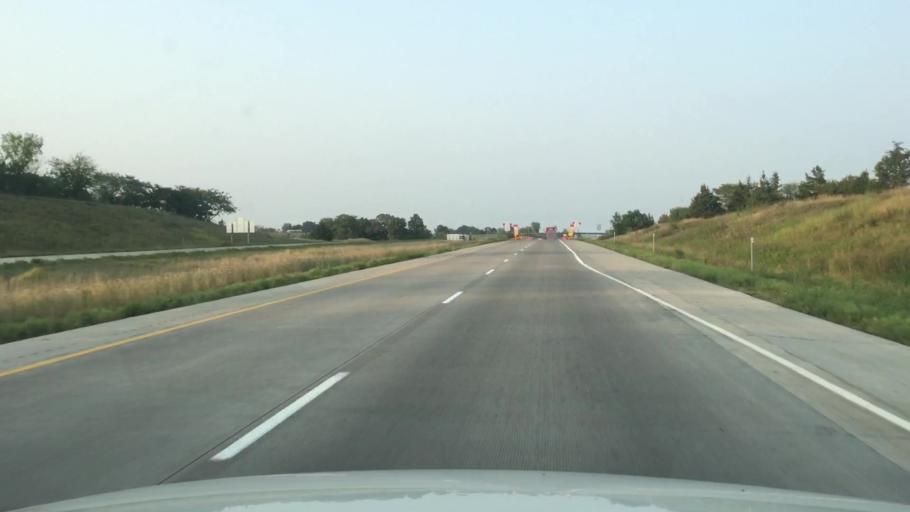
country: US
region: Iowa
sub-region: Decatur County
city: Lamoni
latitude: 40.6292
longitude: -93.8847
